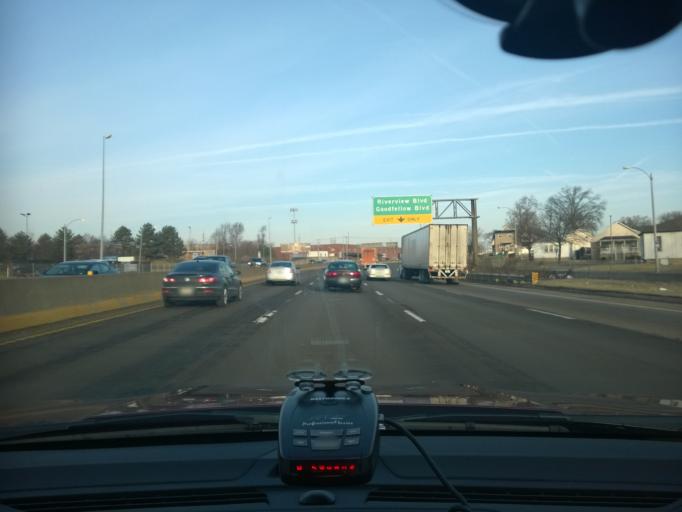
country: US
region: Missouri
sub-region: Saint Louis County
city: Pine Lawn
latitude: 38.6911
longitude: -90.2569
